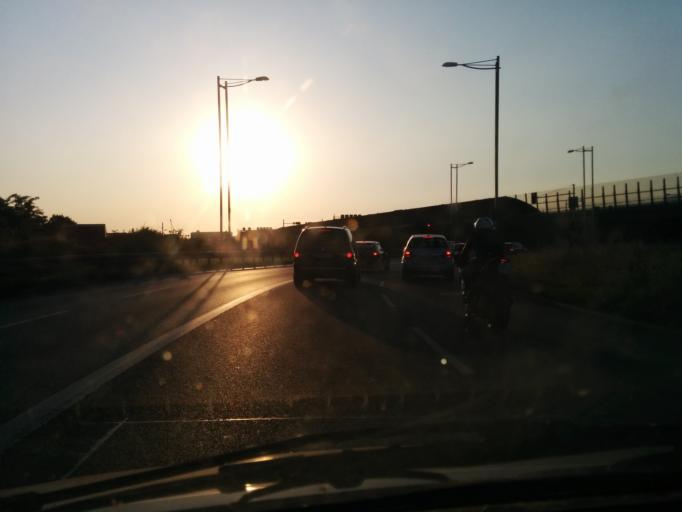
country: DE
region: Berlin
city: Johannisthal
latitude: 52.4273
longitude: 13.5144
